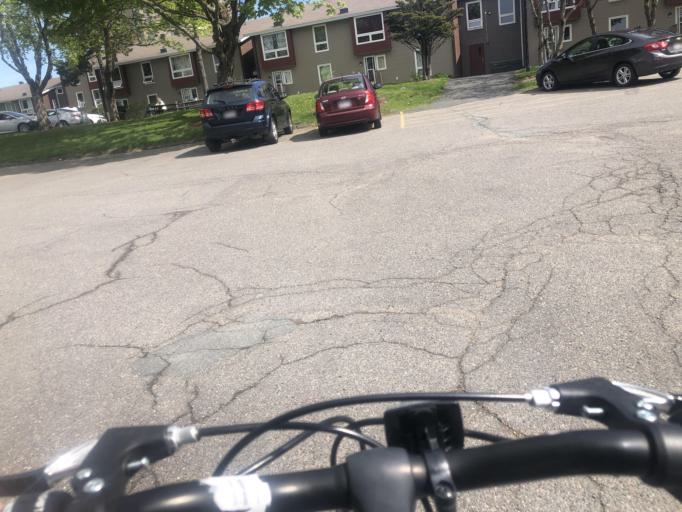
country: CA
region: New Brunswick
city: Saint John
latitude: 45.2814
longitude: -66.0805
